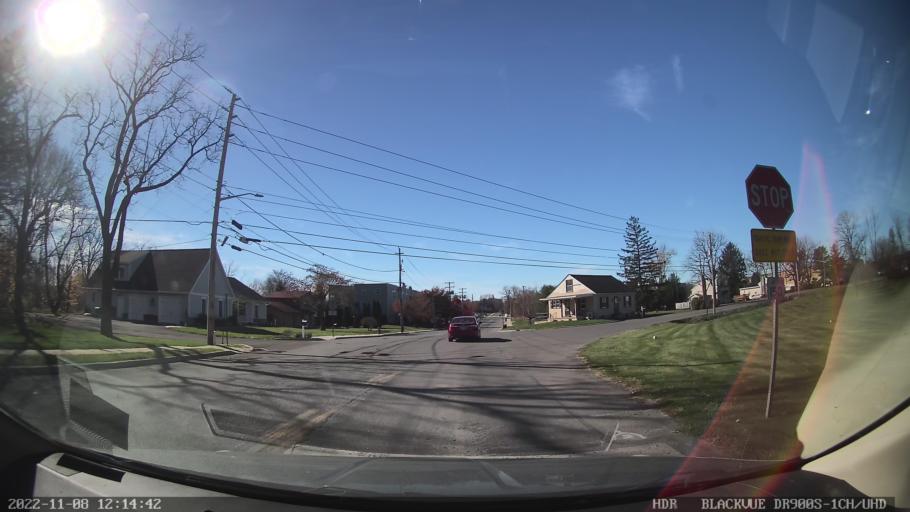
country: US
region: Pennsylvania
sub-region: Berks County
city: Kutztown
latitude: 40.5171
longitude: -75.7675
